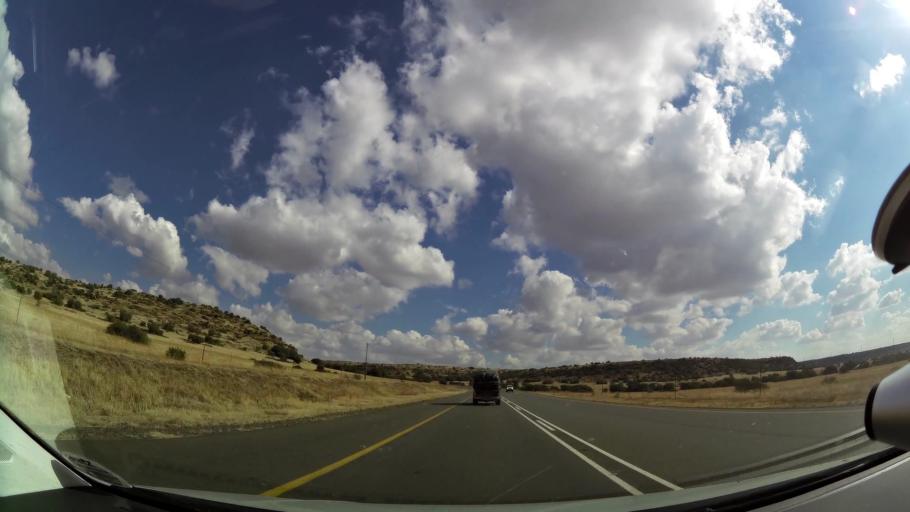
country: ZA
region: Orange Free State
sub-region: Mangaung Metropolitan Municipality
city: Bloemfontein
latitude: -29.1488
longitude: 26.0655
